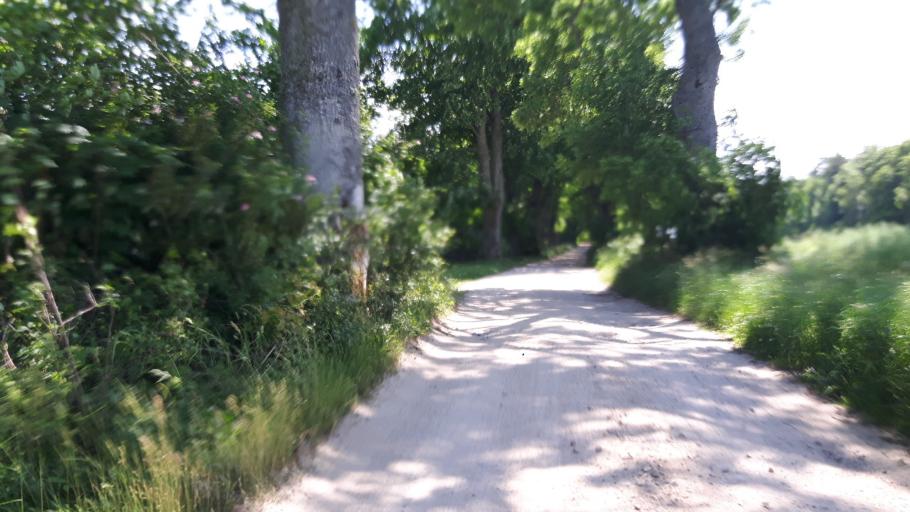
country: PL
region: Pomeranian Voivodeship
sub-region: Powiat wejherowski
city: Choczewo
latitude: 54.7401
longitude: 17.9480
